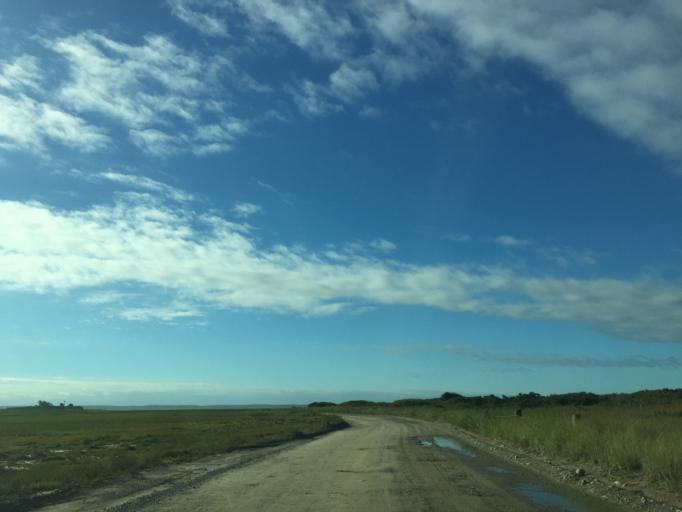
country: US
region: Massachusetts
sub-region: Plymouth County
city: Duxbury
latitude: 42.0079
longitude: -70.6052
